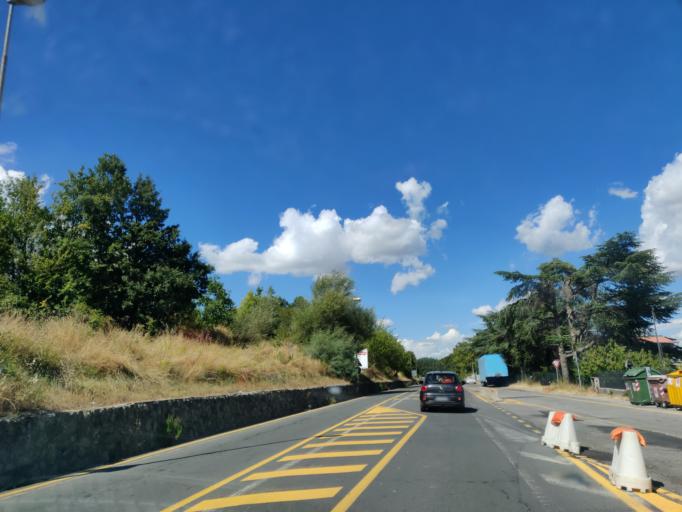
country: IT
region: Tuscany
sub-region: Provincia di Siena
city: Abbadia San Salvatore
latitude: 42.8913
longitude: 11.6669
